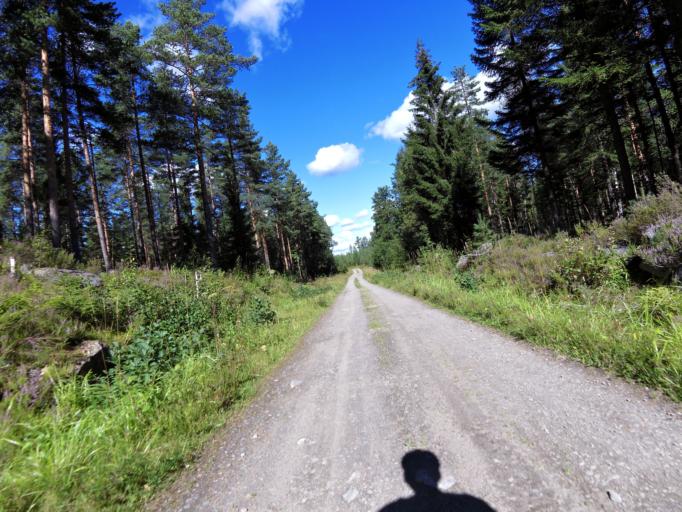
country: SE
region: Gaevleborg
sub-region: Gavle Kommun
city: Valbo
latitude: 60.7469
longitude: 16.9824
